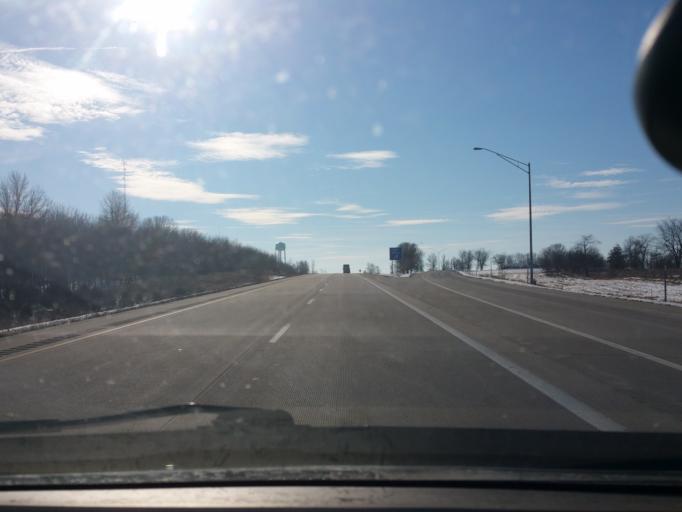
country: US
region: Iowa
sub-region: Clarke County
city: Osceola
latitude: 40.9953
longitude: -93.7995
